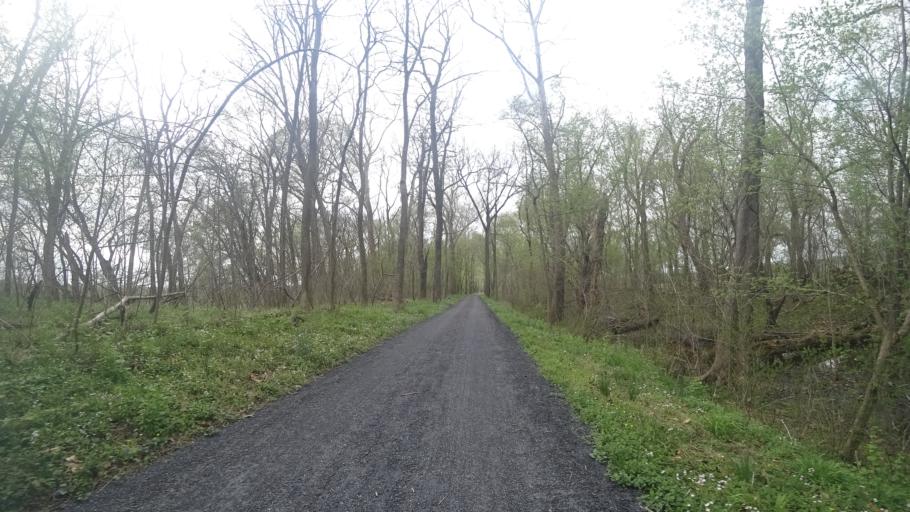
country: US
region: Virginia
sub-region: Loudoun County
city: University Center
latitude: 39.0811
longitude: -77.4480
